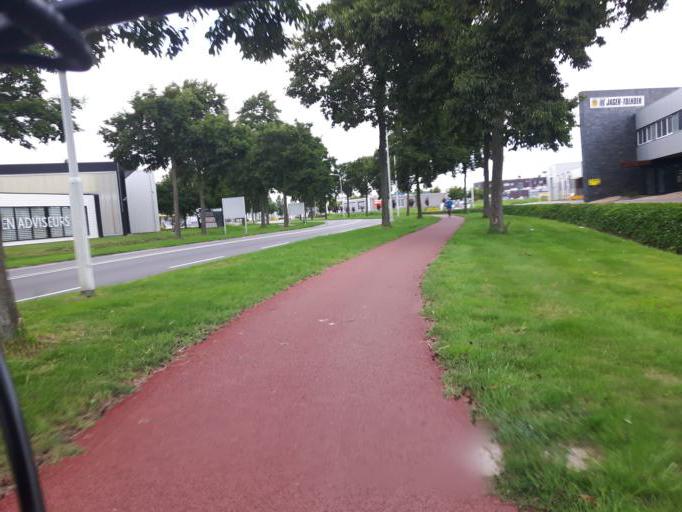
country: NL
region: Zeeland
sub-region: Gemeente Goes
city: Goes
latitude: 51.4894
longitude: 3.8770
